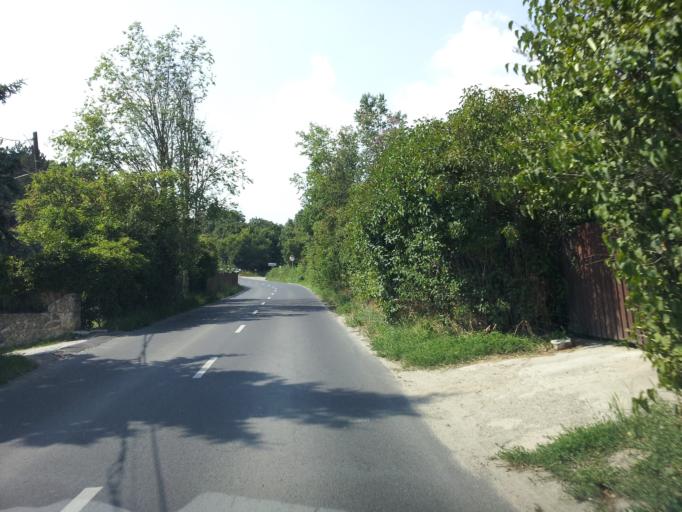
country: HU
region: Veszprem
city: Balatonfured
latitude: 46.9627
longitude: 17.8569
